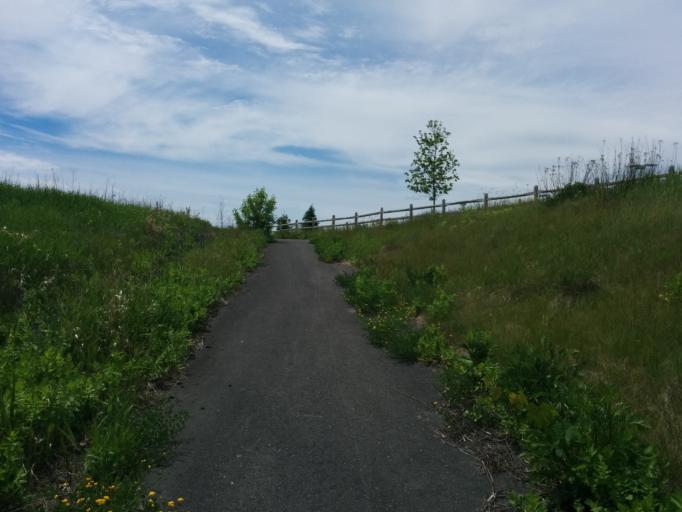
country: CA
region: Ontario
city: Clarence-Rockland
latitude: 45.4783
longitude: -75.4570
